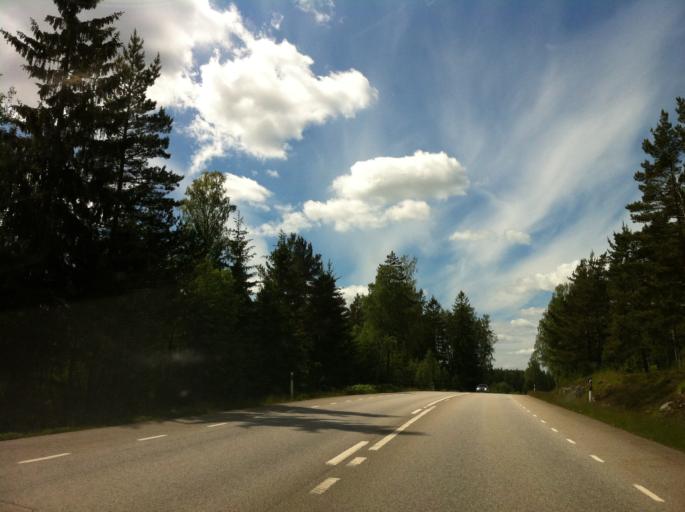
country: SE
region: Vaestra Goetaland
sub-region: Amals Kommun
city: Amal
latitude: 58.9908
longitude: 12.6705
